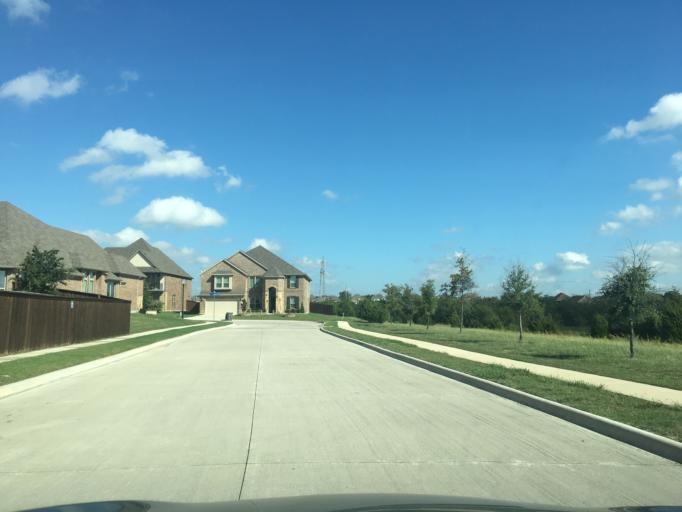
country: US
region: Texas
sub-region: Dallas County
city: Sachse
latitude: 32.9632
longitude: -96.5723
